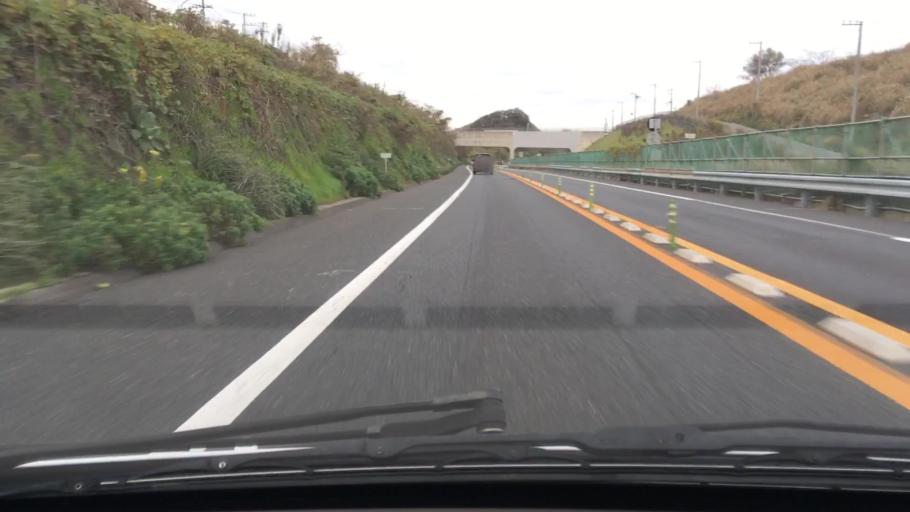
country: JP
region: Chiba
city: Kimitsu
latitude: 35.2387
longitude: 139.8883
